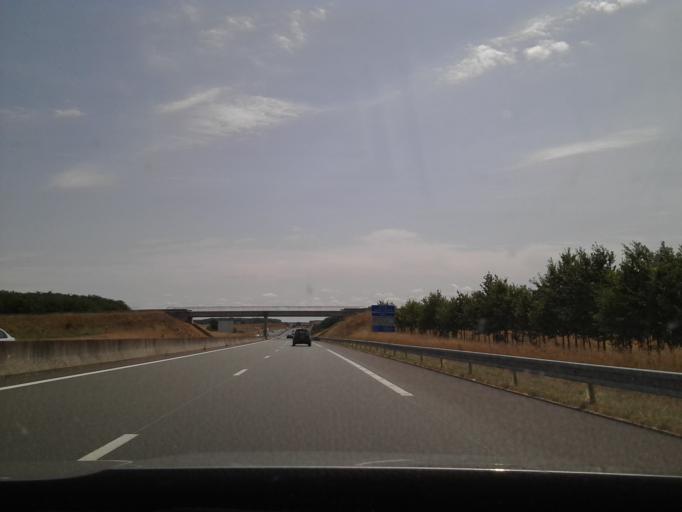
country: FR
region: Centre
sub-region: Departement d'Indre-et-Loire
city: Saint-Christophe-sur-le-Nais
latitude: 47.6515
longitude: 0.4555
